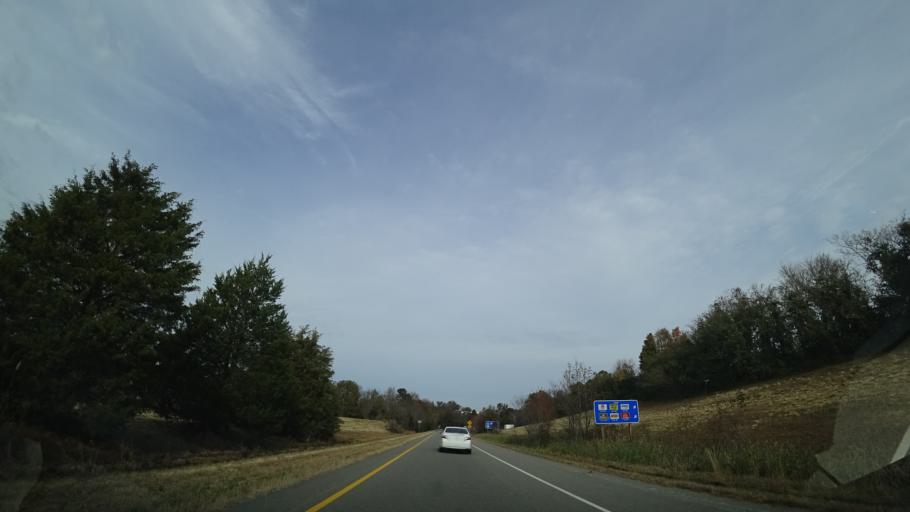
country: US
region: Virginia
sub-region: Hanover County
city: Mechanicsville
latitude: 37.6059
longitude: -77.3573
